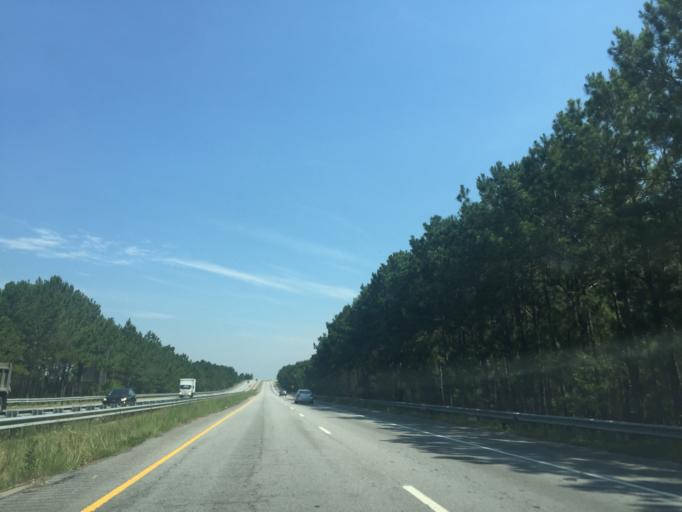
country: US
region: Georgia
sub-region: Chatham County
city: Georgetown
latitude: 31.9931
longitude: -81.1997
